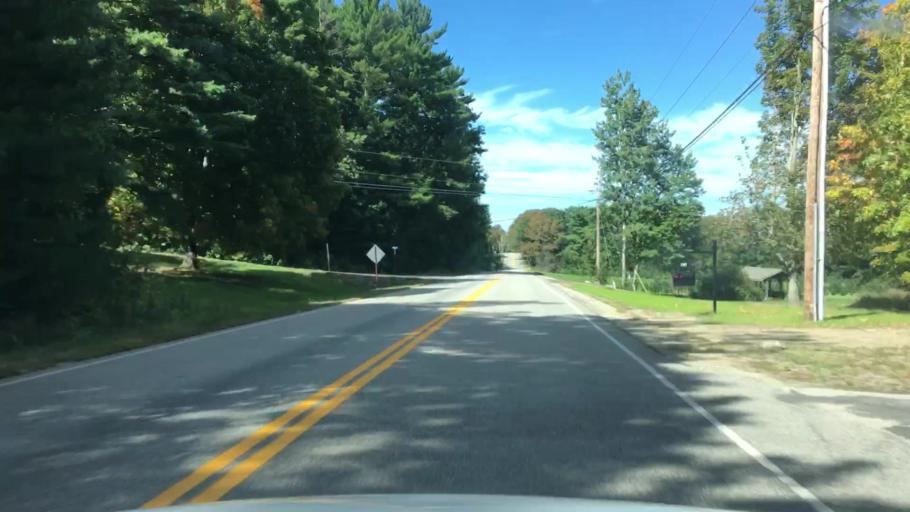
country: US
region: Maine
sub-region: Cumberland County
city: West Scarborough
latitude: 43.6155
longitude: -70.4057
